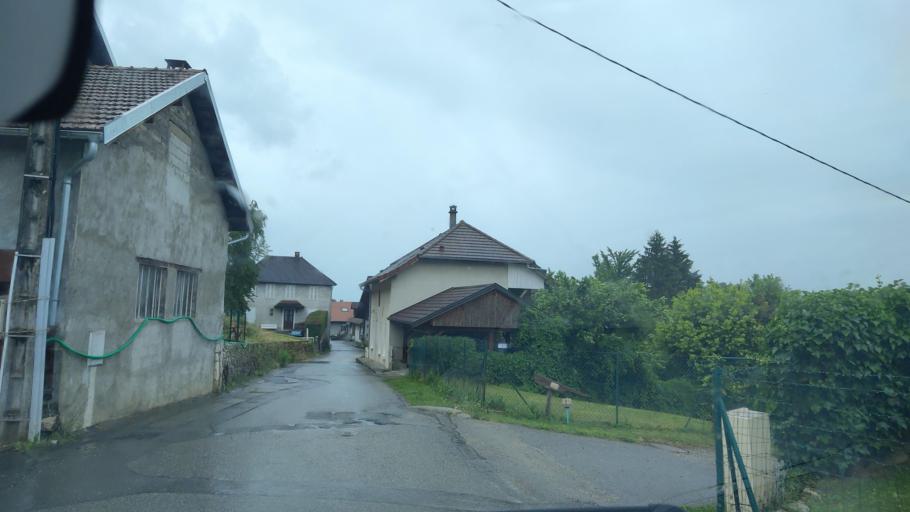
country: FR
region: Rhone-Alpes
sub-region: Departement de la Savoie
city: Chindrieux
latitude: 45.8207
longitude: 5.8527
